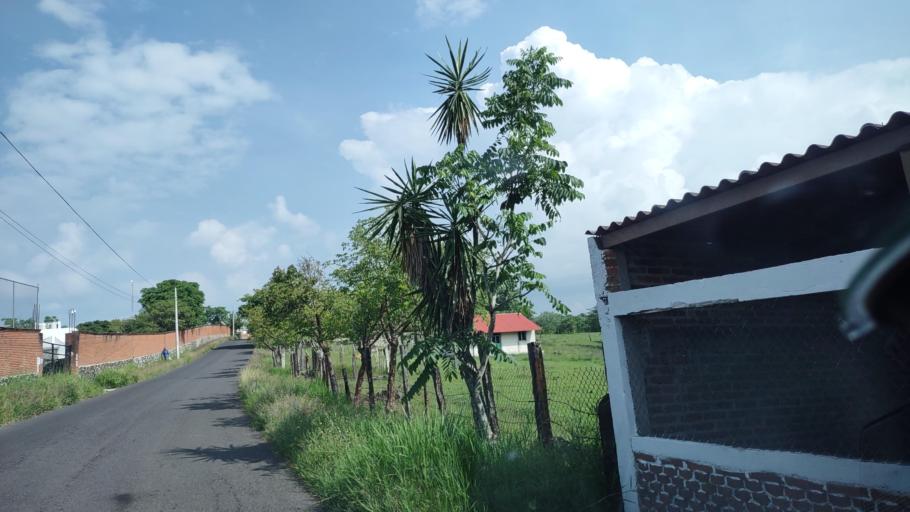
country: MX
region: Veracruz
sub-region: Coatepec
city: Bella Esperanza
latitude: 19.4526
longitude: -96.8302
